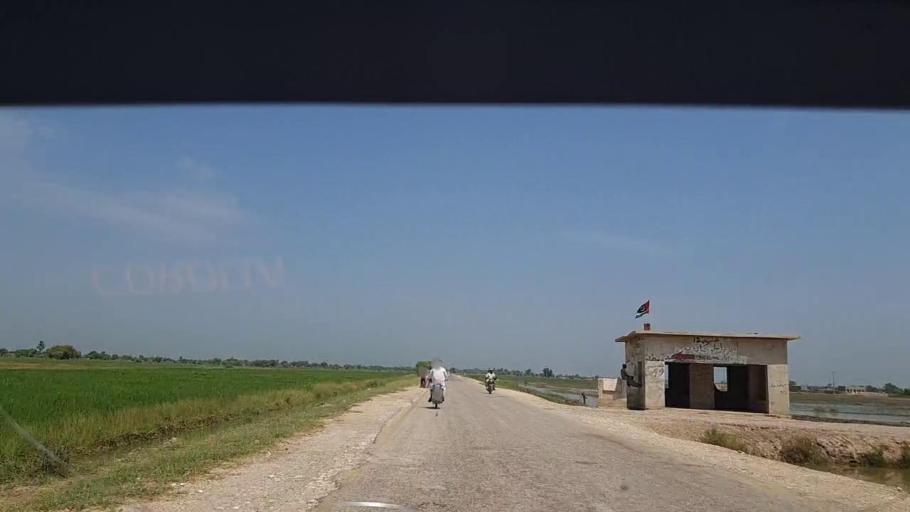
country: PK
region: Sindh
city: Rustam jo Goth
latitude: 28.0972
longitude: 68.8016
